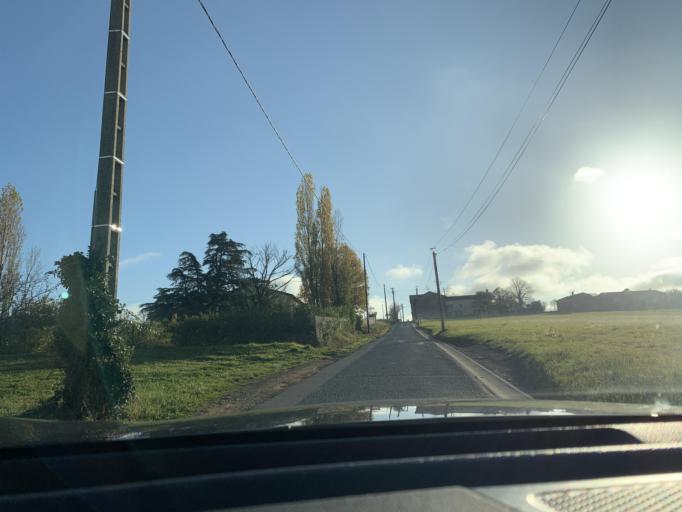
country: FR
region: Rhone-Alpes
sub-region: Departement du Rhone
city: Pommiers
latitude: 45.9448
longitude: 4.6874
